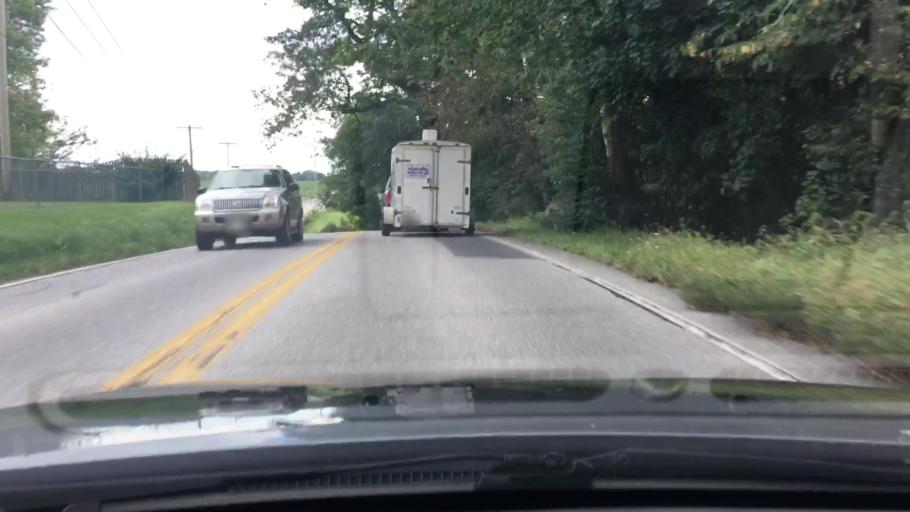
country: US
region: Pennsylvania
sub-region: Franklin County
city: Scotland
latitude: 39.9628
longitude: -77.5839
